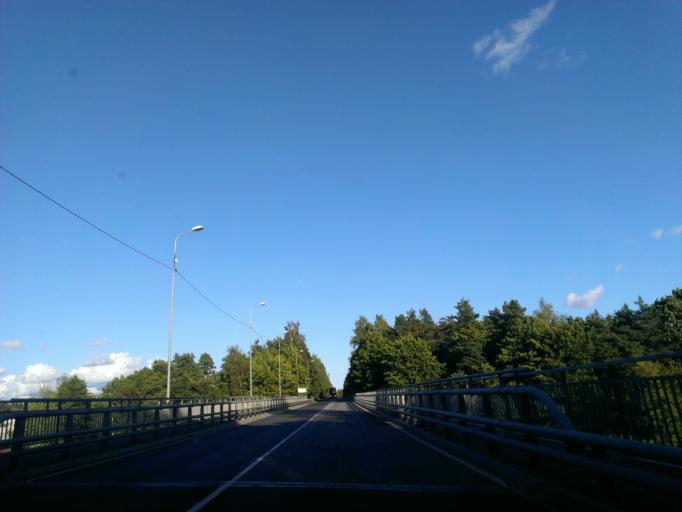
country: LV
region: Riga
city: Bergi
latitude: 57.0031
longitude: 24.2667
